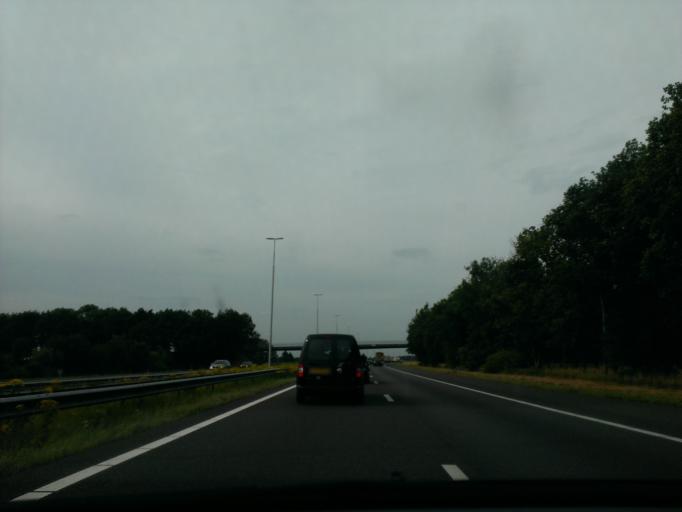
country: NL
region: Gelderland
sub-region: Gemeente Epe
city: Vaassen
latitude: 52.2649
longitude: 6.0018
